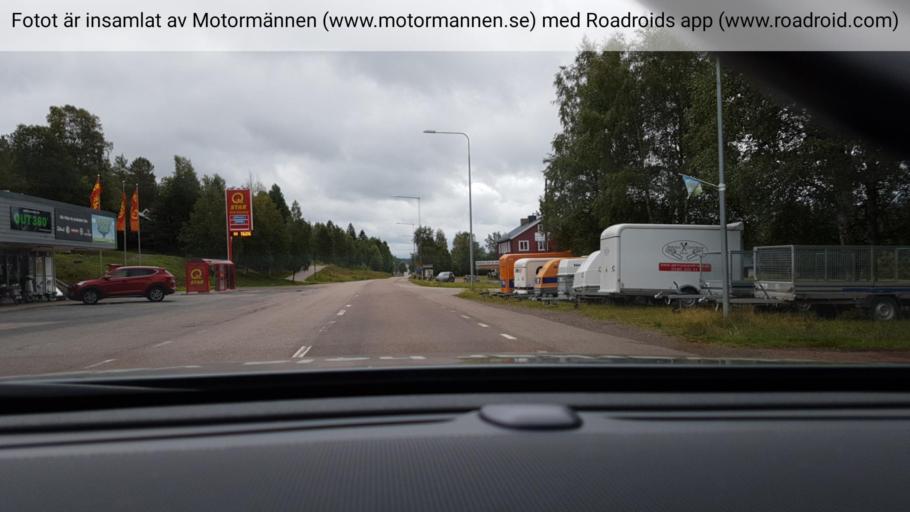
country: SE
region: Dalarna
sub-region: Malung-Saelens kommun
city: Malung
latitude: 61.1620
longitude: 13.2623
